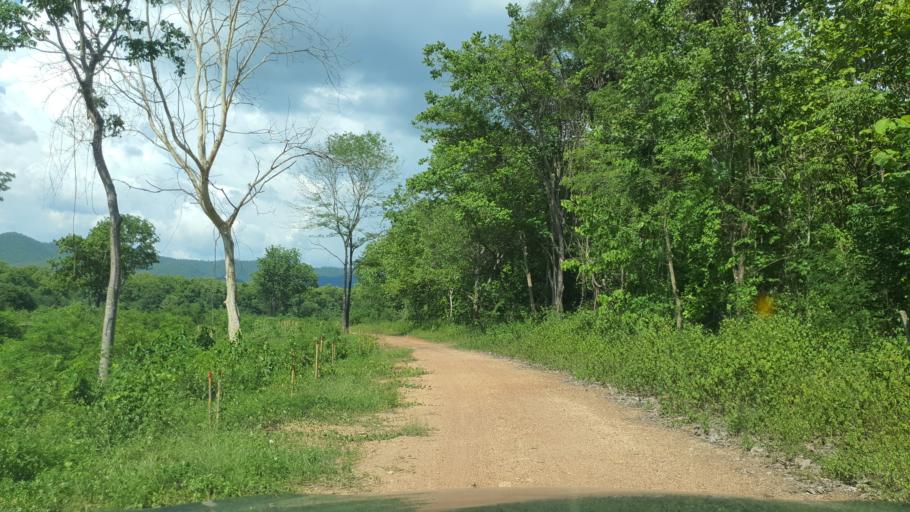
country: TH
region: Chiang Mai
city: Mae Taeng
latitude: 19.0893
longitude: 99.0797
